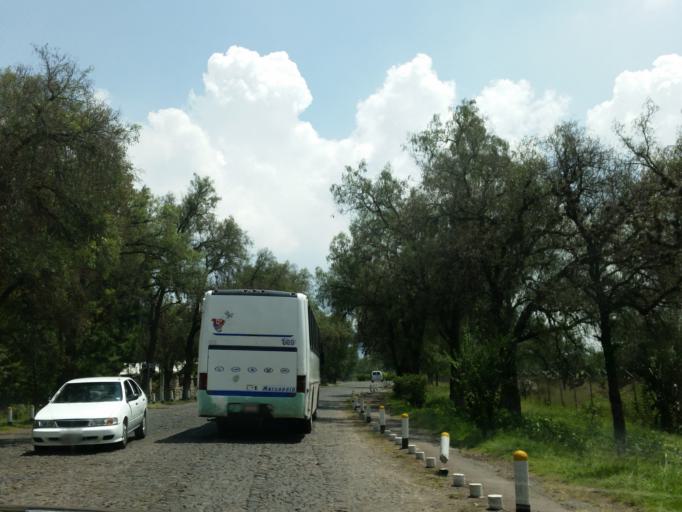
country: MX
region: Mexico
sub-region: Teotihuacan
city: Teotihuacan de Arista
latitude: 19.6885
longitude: -98.8513
